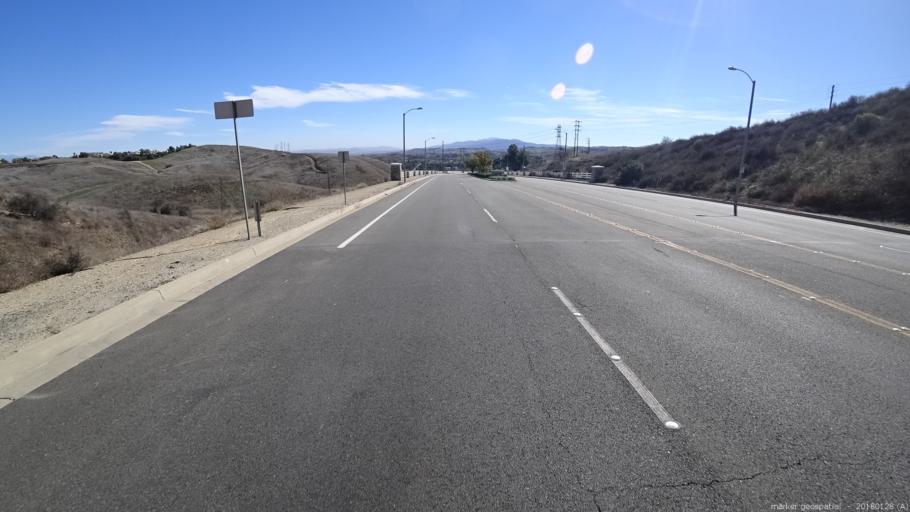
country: US
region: California
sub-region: San Bernardino County
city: Chino Hills
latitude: 34.0047
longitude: -117.7700
